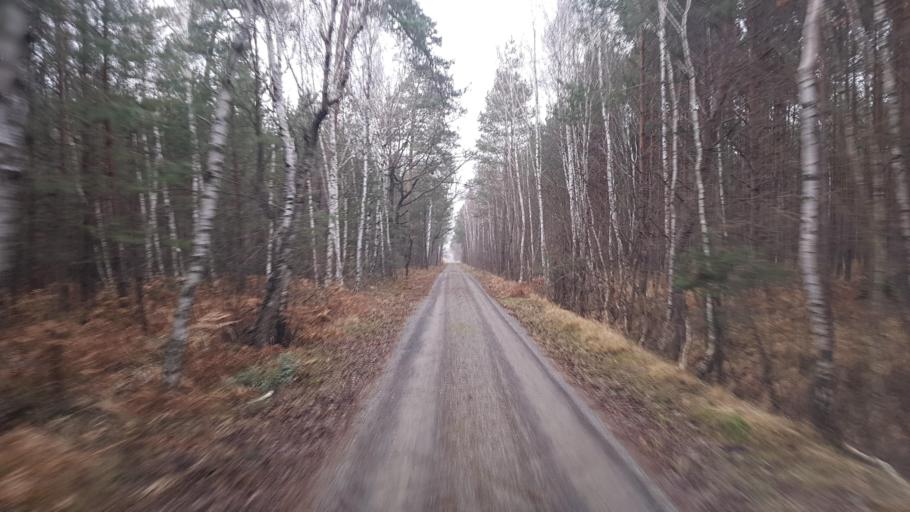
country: DE
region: Brandenburg
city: Plessa
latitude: 51.5214
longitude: 13.6282
